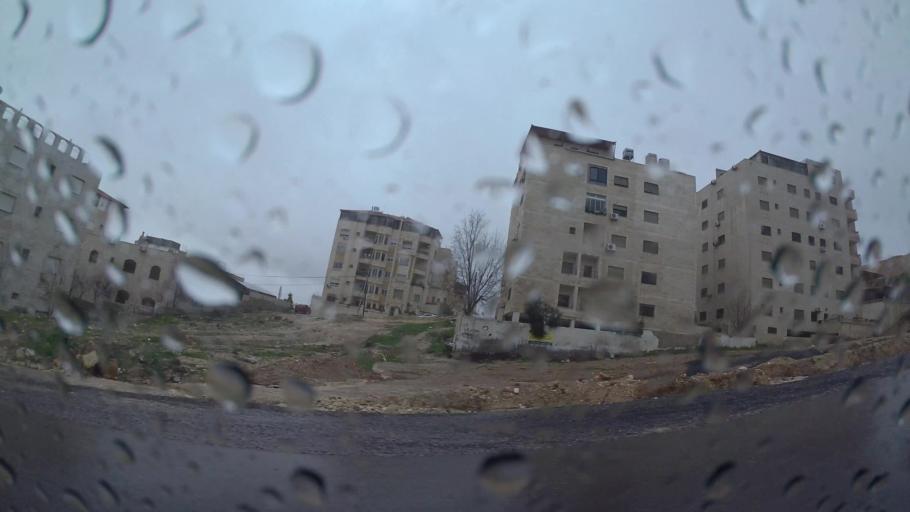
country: JO
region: Amman
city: Al Jubayhah
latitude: 32.0231
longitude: 35.8888
